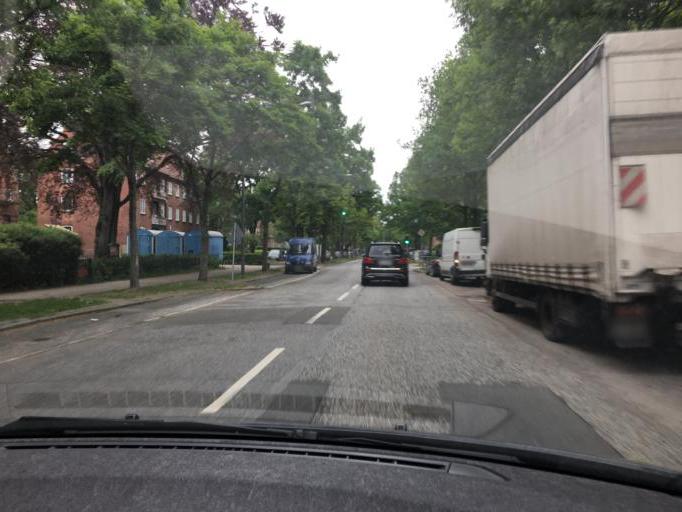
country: DE
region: Hamburg
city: Kleiner Grasbrook
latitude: 53.5114
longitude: 9.9928
